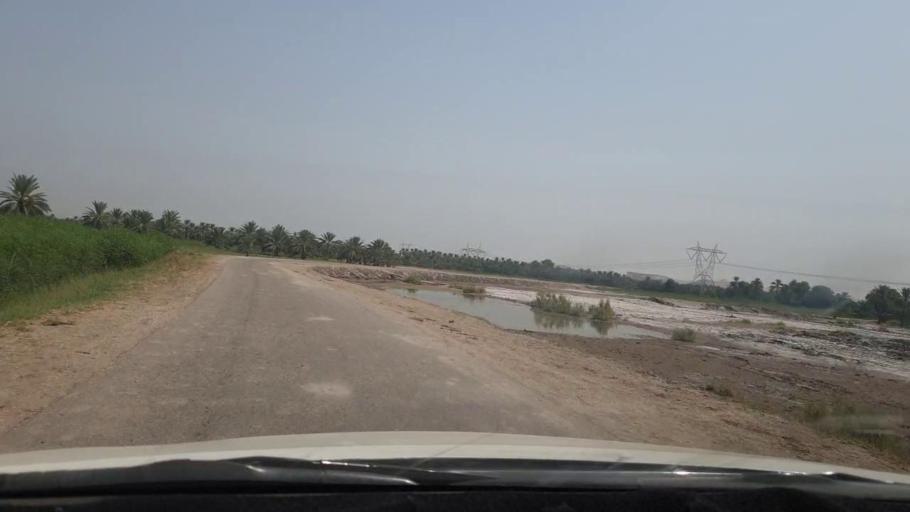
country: PK
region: Sindh
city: Rohri
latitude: 27.5959
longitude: 68.9025
